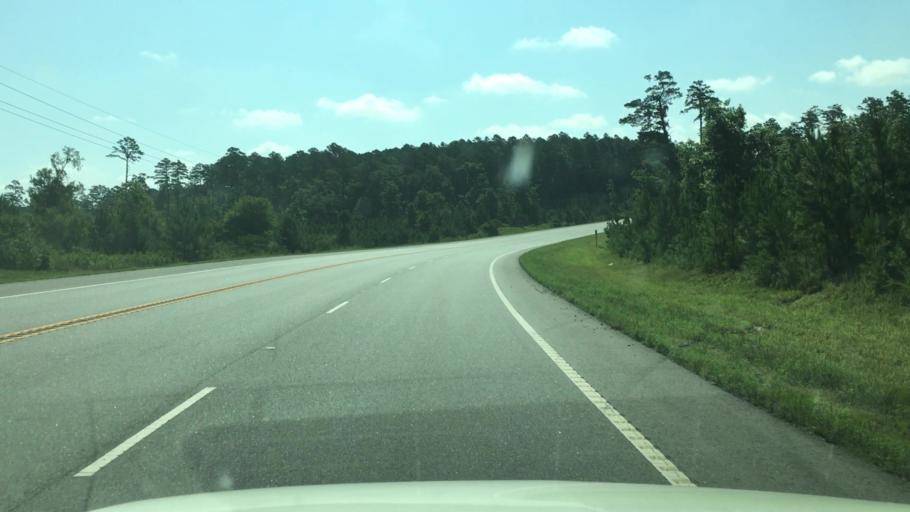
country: US
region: Arkansas
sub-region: Garland County
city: Piney
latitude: 34.5227
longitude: -93.3200
